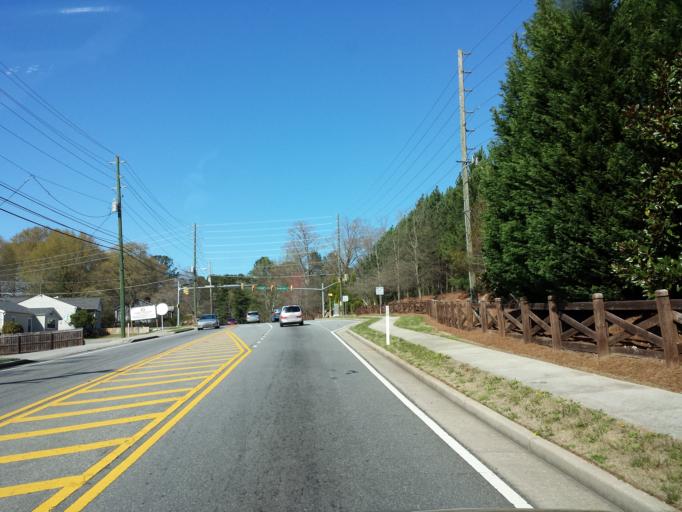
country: US
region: Georgia
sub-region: Cobb County
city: Fair Oaks
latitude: 33.9226
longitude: -84.5557
